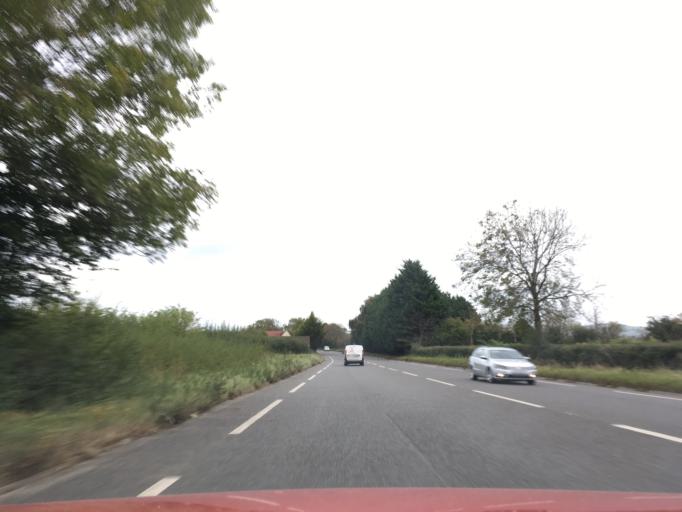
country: GB
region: England
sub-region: Gloucestershire
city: Dursley
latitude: 51.7362
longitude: -2.3608
